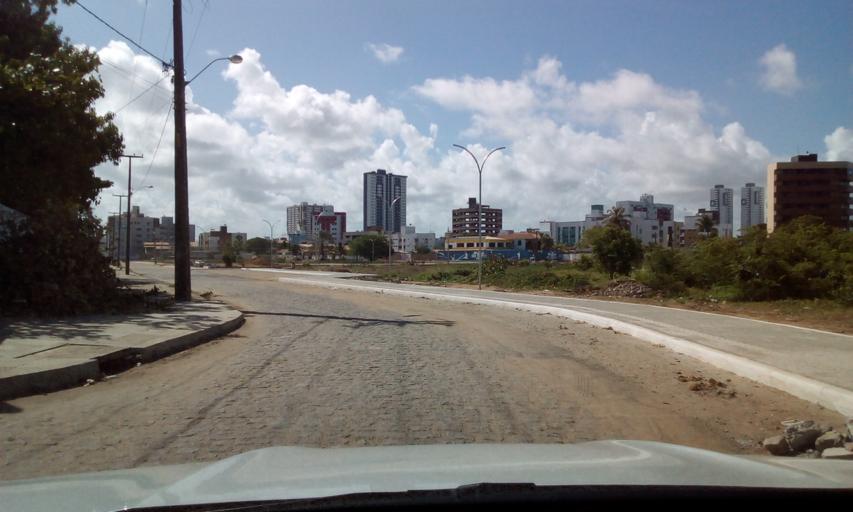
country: BR
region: Paraiba
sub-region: Joao Pessoa
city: Joao Pessoa
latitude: -7.0796
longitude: -34.8350
